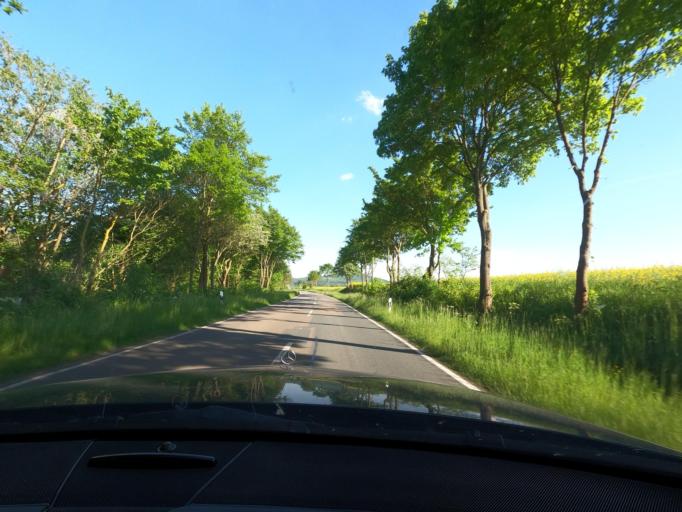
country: DE
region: Hesse
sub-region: Regierungsbezirk Kassel
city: Martinhagen
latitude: 51.3248
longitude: 9.2527
